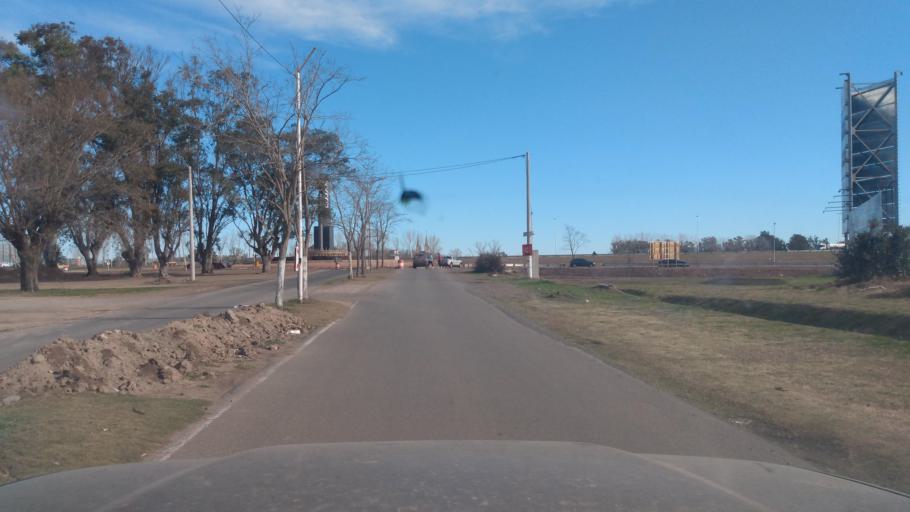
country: AR
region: Buenos Aires
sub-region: Partido de Lujan
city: Lujan
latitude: -34.5479
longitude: -59.1126
